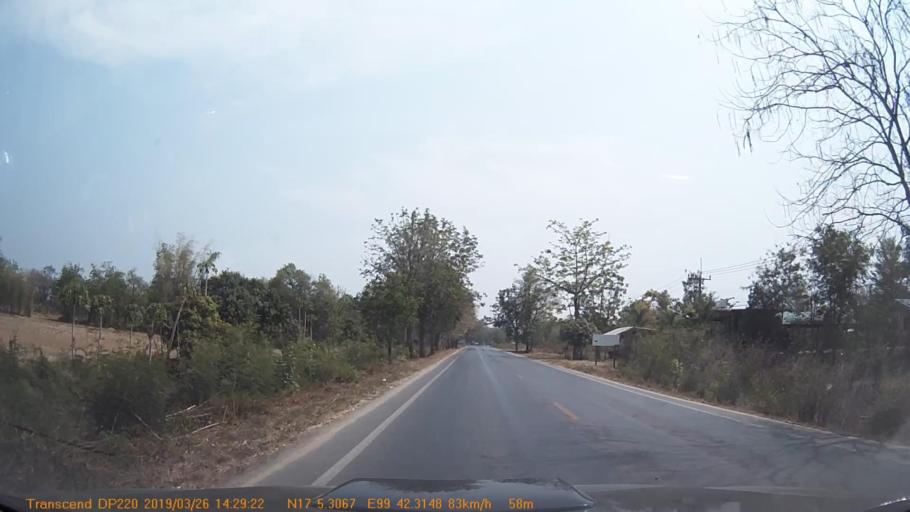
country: TH
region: Sukhothai
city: Ban Na
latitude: 17.0881
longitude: 99.7053
